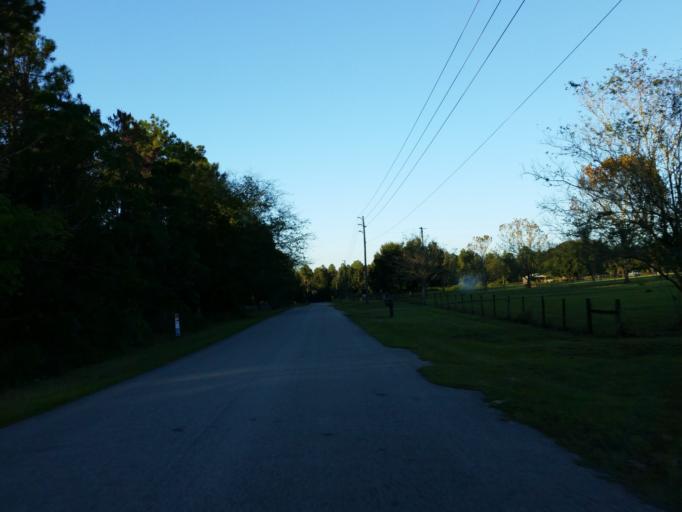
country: US
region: Florida
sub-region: Hernando County
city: Hill 'n Dale
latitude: 28.4532
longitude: -82.2698
